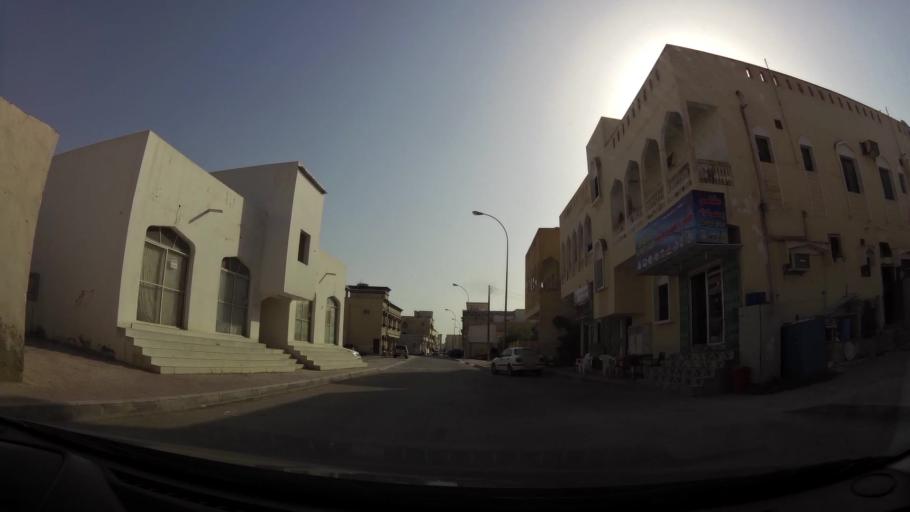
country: OM
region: Zufar
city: Salalah
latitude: 17.0072
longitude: 54.0739
